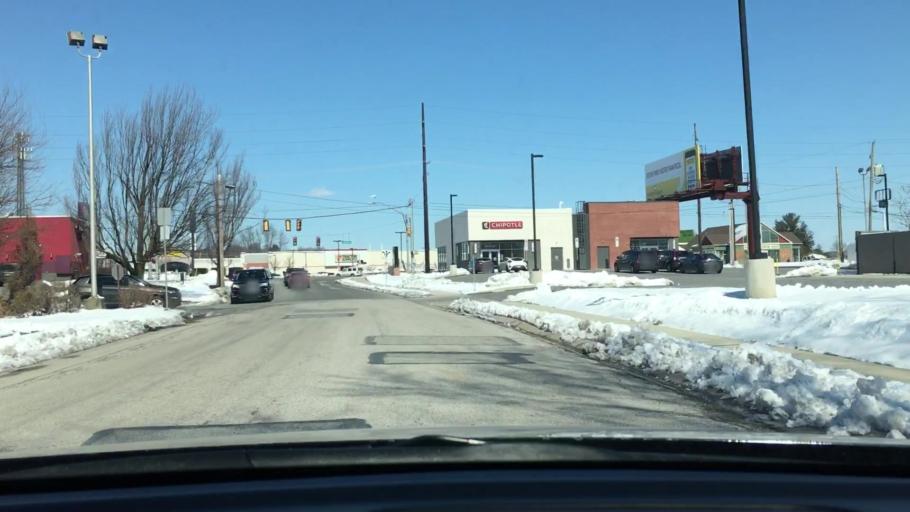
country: US
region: Pennsylvania
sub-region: York County
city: North York
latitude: 39.9789
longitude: -76.7519
